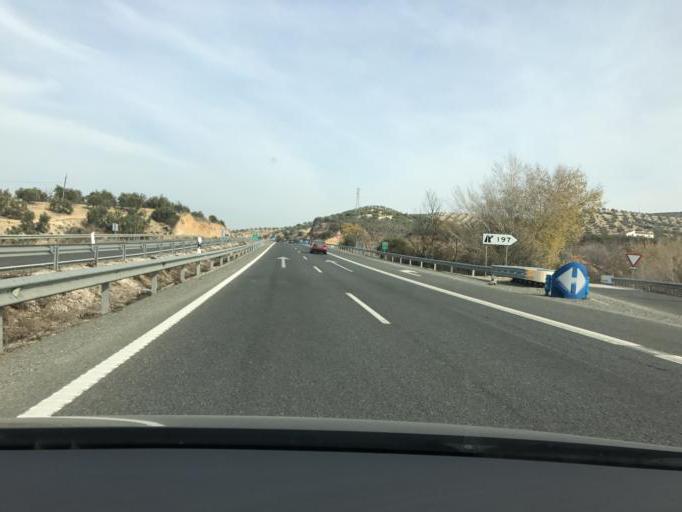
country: ES
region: Andalusia
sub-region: Provincia de Granada
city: Salar
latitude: 37.1683
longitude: -4.0864
